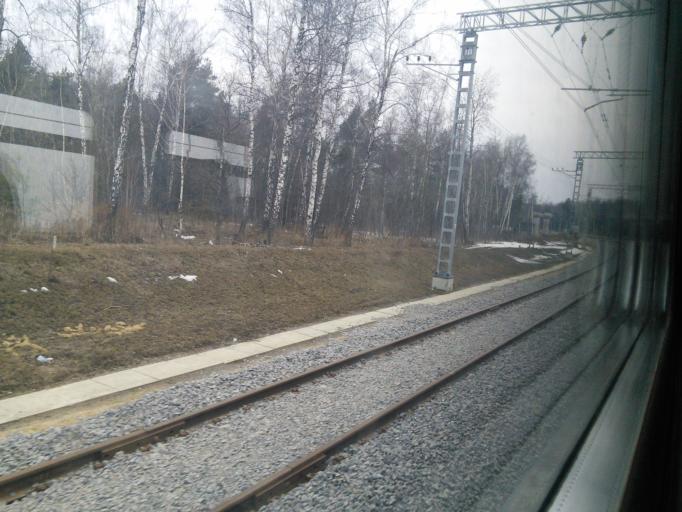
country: RU
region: Moskovskaya
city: Yakovlevskoye
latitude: 55.4331
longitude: 37.8759
